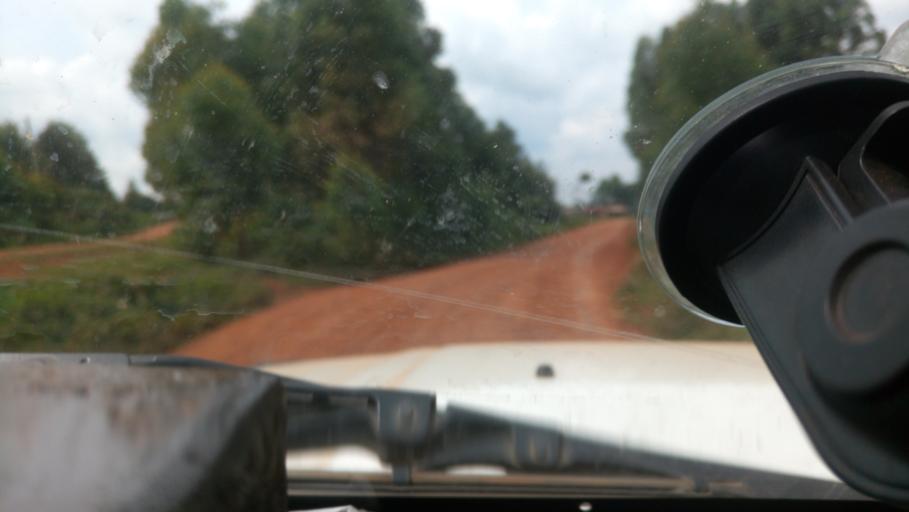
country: KE
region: Nyamira District
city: Keroka
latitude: -0.7588
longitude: 34.8881
